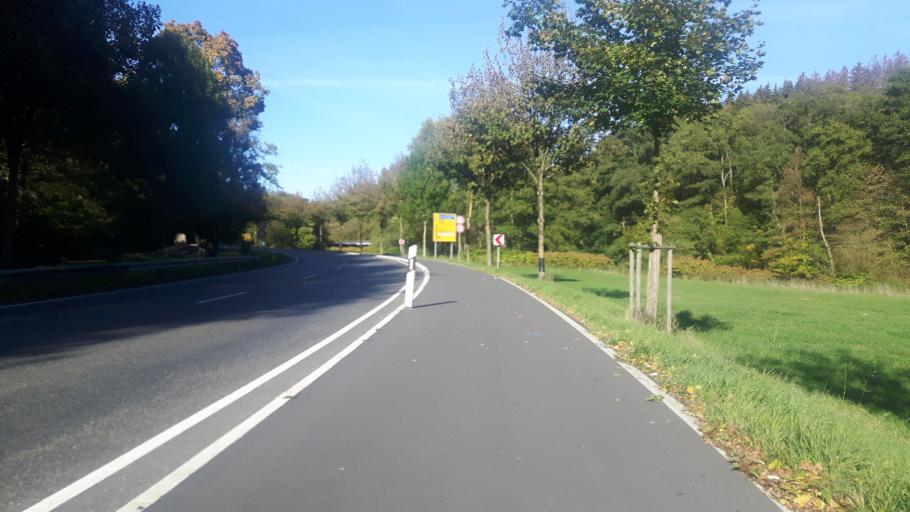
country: DE
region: Rheinland-Pfalz
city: Mittelhof
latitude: 50.7867
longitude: 7.7925
